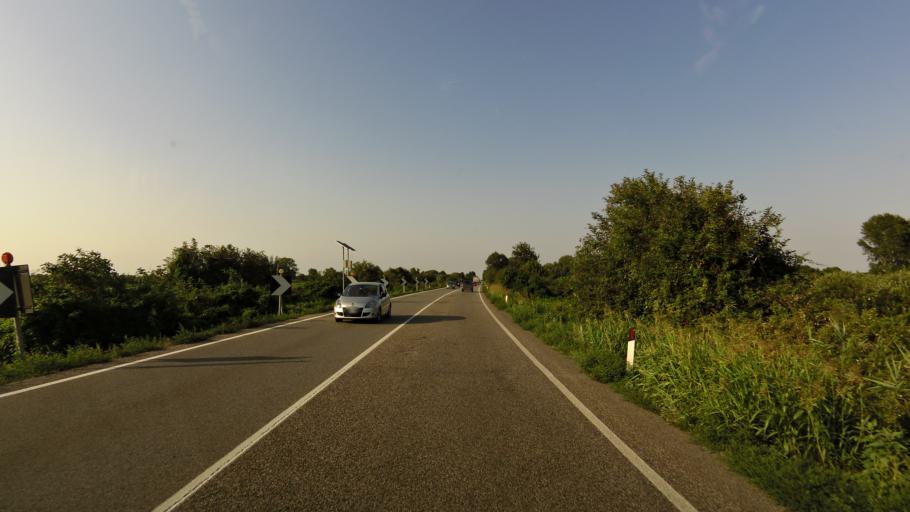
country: IT
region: Emilia-Romagna
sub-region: Provincia di Ravenna
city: Marina Romea
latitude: 44.5405
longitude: 12.2348
